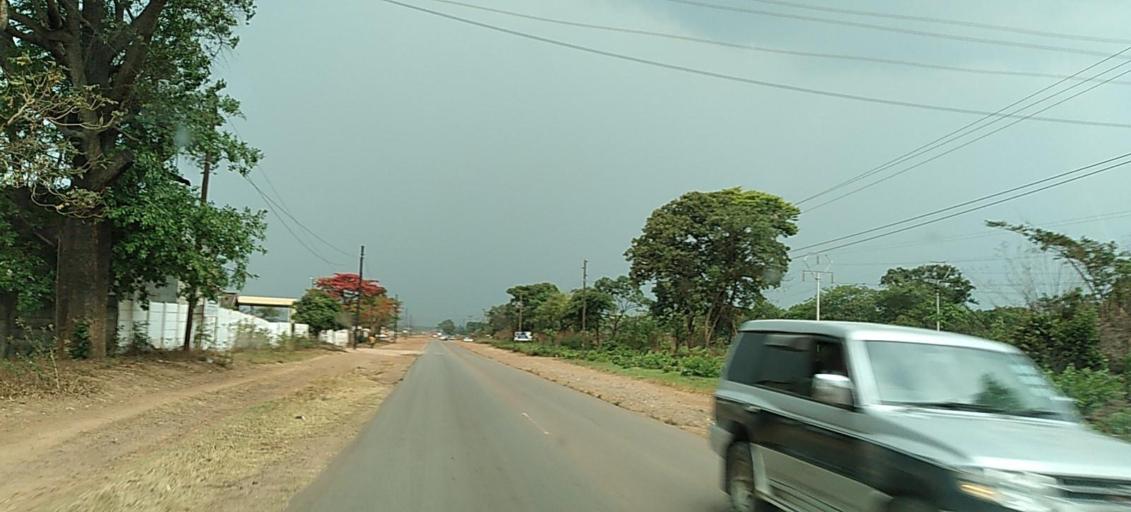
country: ZM
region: Copperbelt
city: Kalulushi
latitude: -12.8333
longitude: 28.1075
